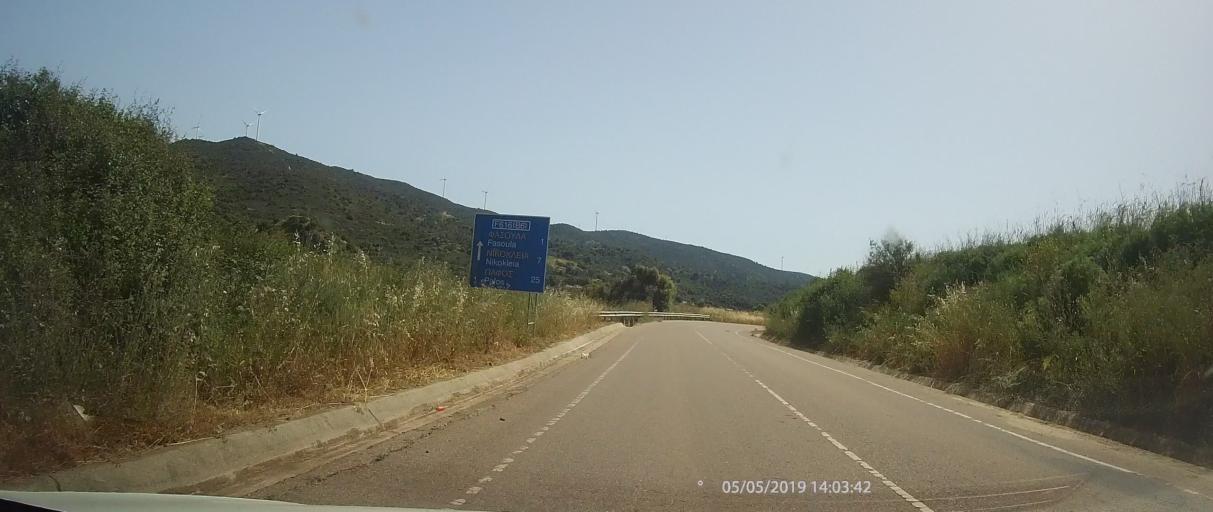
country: CY
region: Limassol
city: Pissouri
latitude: 34.7654
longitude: 32.6332
